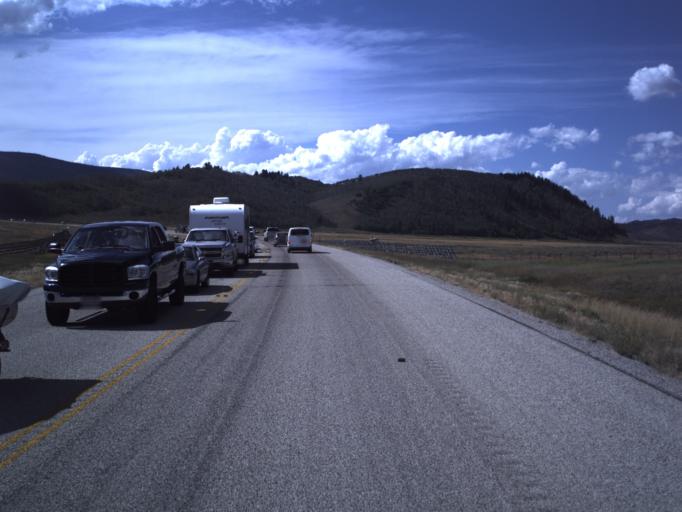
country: US
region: Utah
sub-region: Wasatch County
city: Heber
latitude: 40.2768
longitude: -111.2158
